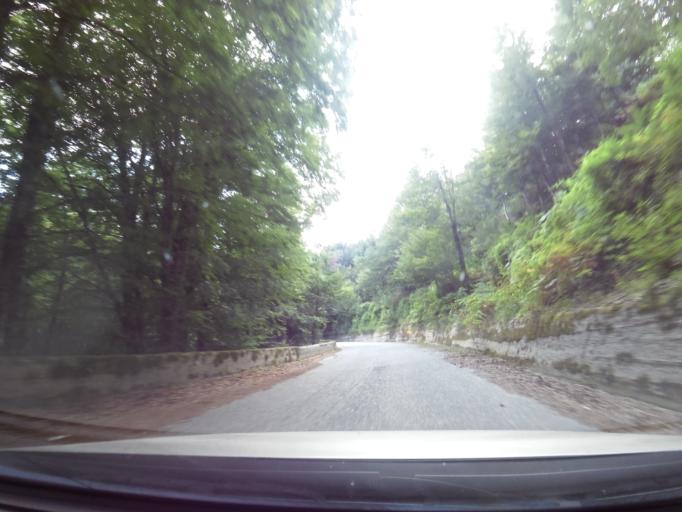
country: IT
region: Calabria
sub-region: Provincia di Vibo-Valentia
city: Nardodipace
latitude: 38.5061
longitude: 16.3770
